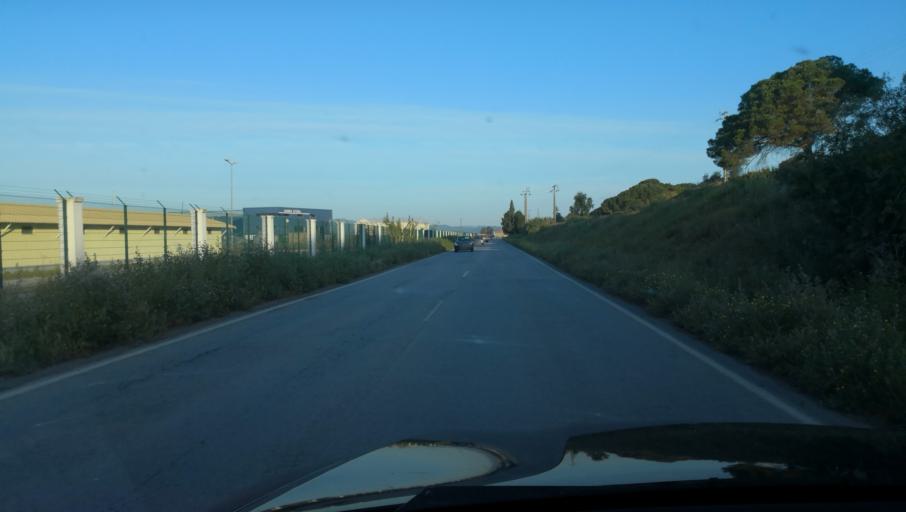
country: PT
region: Setubal
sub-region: Setubal
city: Setubal
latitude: 38.4921
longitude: -8.8220
